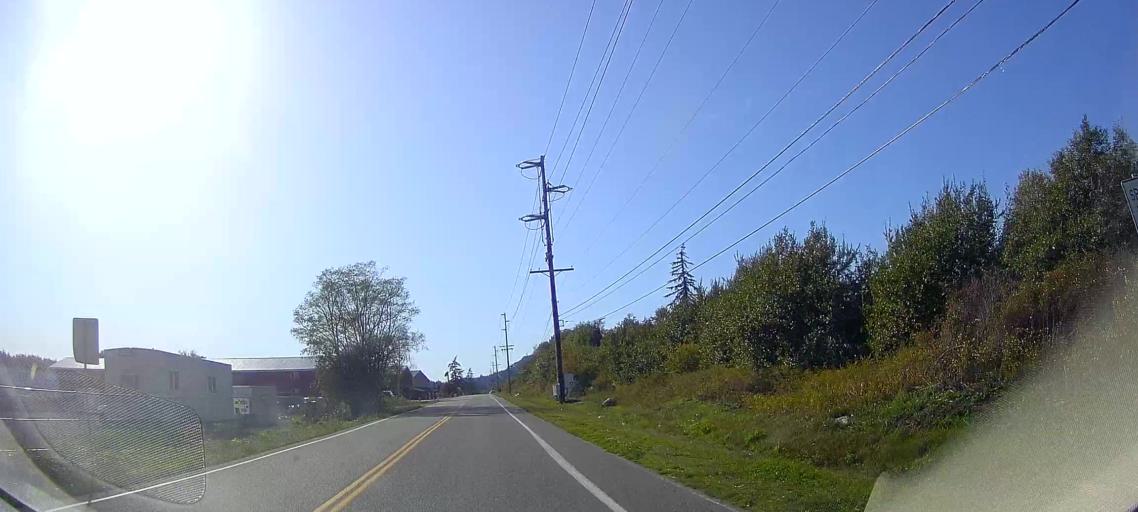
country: US
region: Washington
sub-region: Skagit County
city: Anacortes
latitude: 48.4643
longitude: -122.5447
